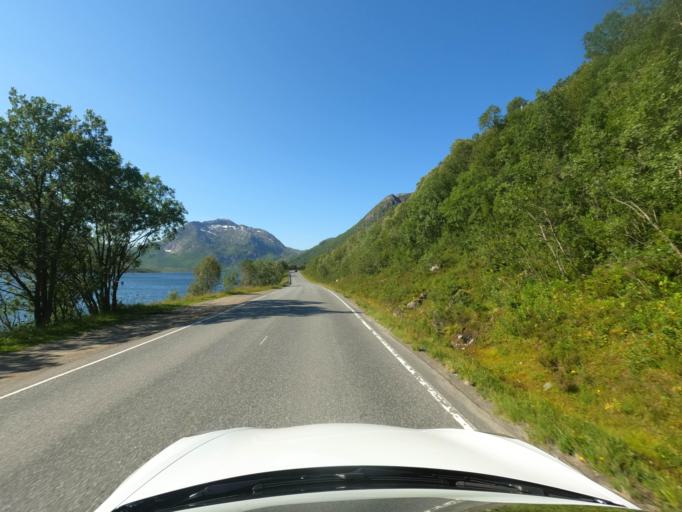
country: NO
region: Nordland
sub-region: Lodingen
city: Lodingen
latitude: 68.5609
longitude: 15.7788
